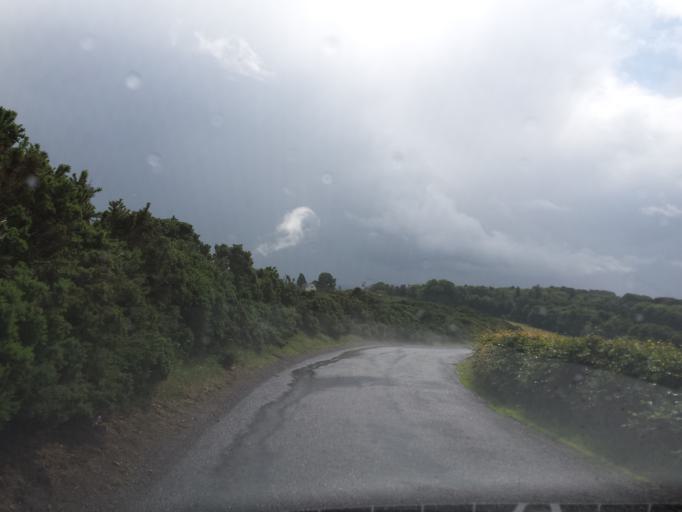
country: GB
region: Scotland
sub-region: The Scottish Borders
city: Saint Boswells
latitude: 55.5985
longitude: -2.6462
